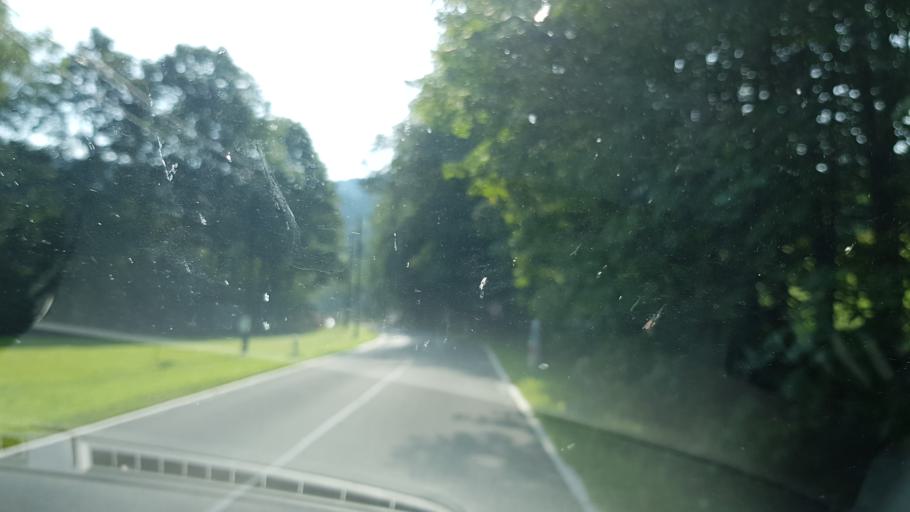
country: CZ
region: Olomoucky
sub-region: Okres Jesenik
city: Jesenik
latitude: 50.2071
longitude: 17.2322
